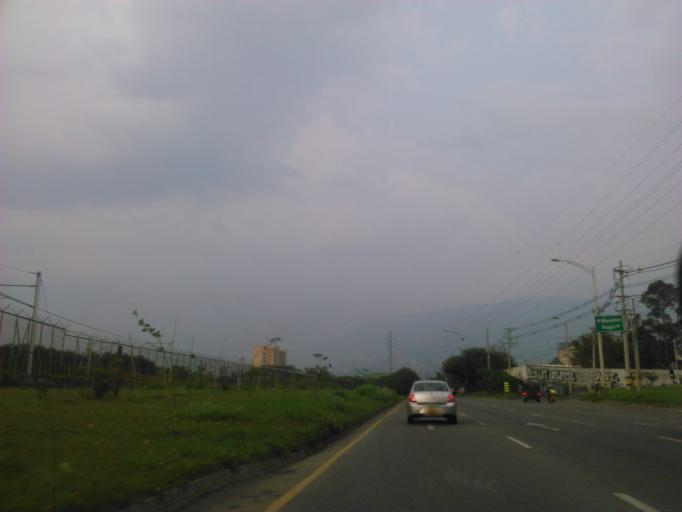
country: CO
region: Antioquia
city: Sabaneta
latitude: 6.1601
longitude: -75.6115
